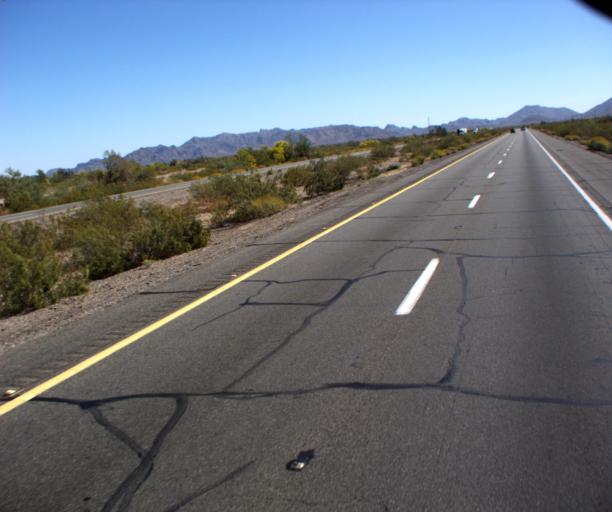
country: US
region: Arizona
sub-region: La Paz County
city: Quartzsite
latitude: 33.6681
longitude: -114.1751
